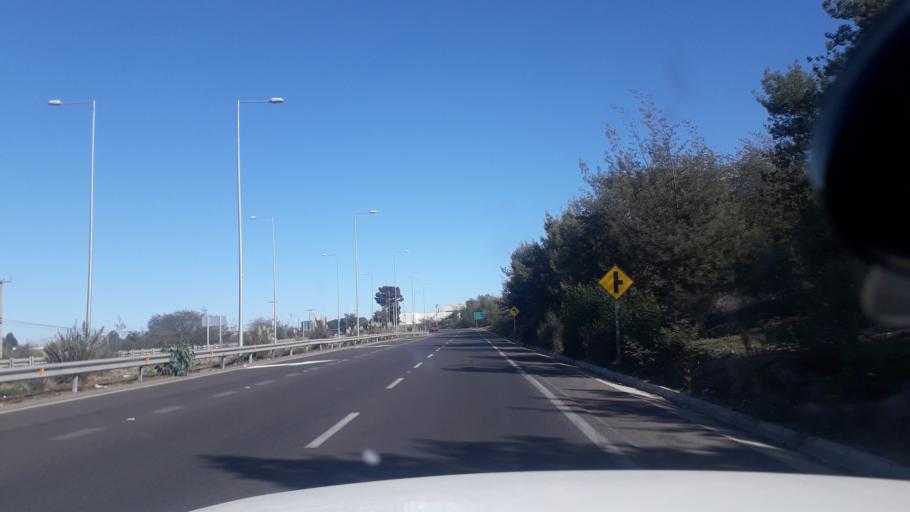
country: CL
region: Valparaiso
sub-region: Provincia de Valparaiso
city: Vina del Mar
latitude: -32.9553
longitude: -71.5097
